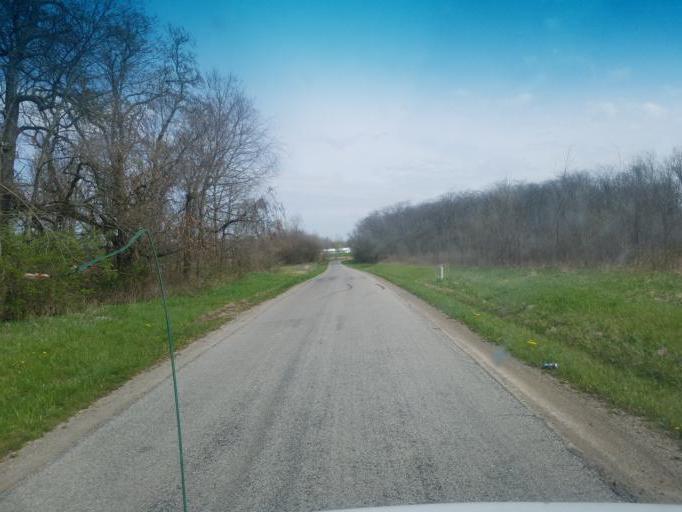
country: US
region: Ohio
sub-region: Union County
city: Richwood
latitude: 40.4787
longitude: -83.4337
